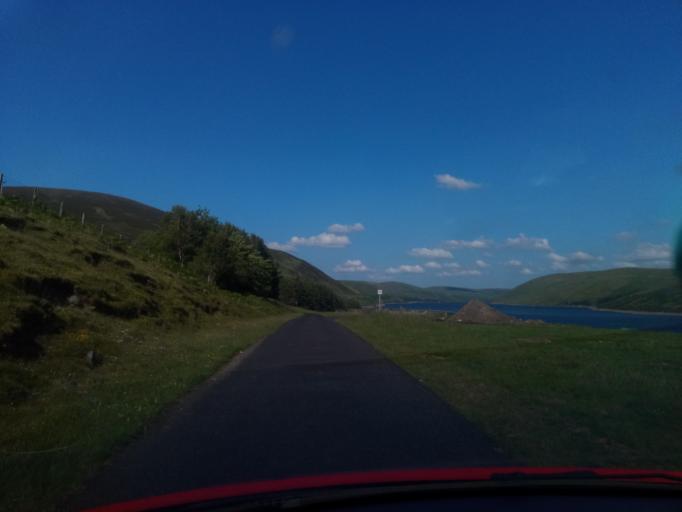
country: GB
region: Scotland
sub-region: Dumfries and Galloway
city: Moffat
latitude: 55.4804
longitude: -3.3068
